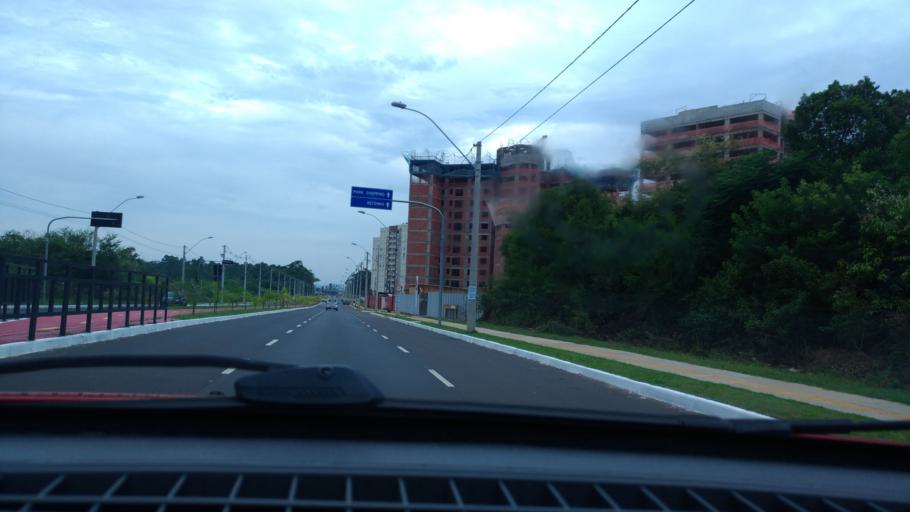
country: BR
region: Rio Grande do Sul
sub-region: Canoas
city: Canoas
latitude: -29.9061
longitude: -51.1649
